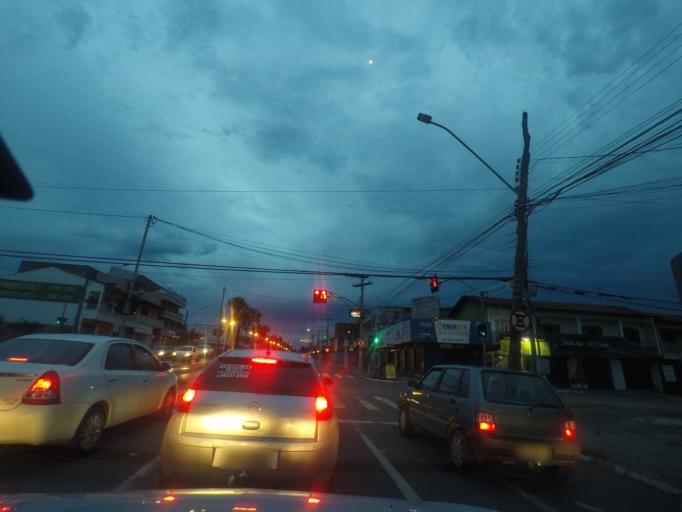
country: BR
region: Goias
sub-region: Goiania
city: Goiania
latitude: -16.7202
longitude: -49.3008
